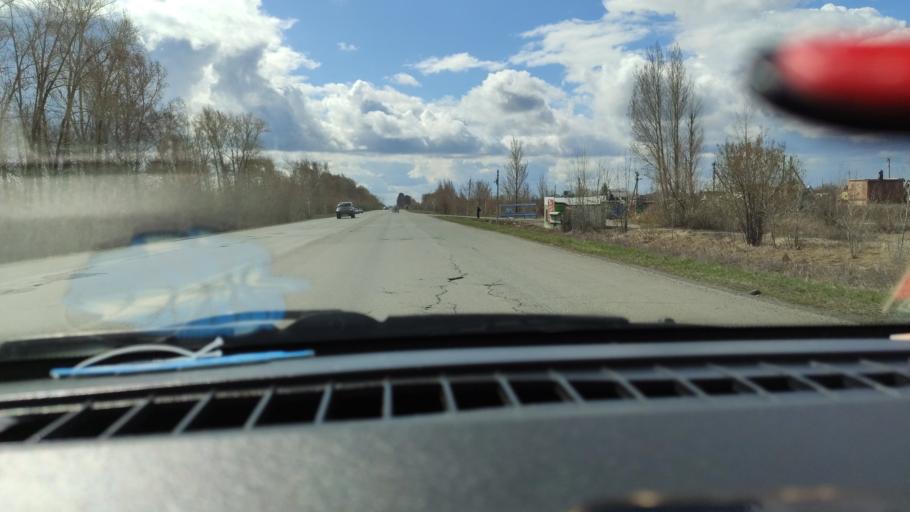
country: RU
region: Samara
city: Tol'yatti
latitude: 53.6996
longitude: 49.4204
